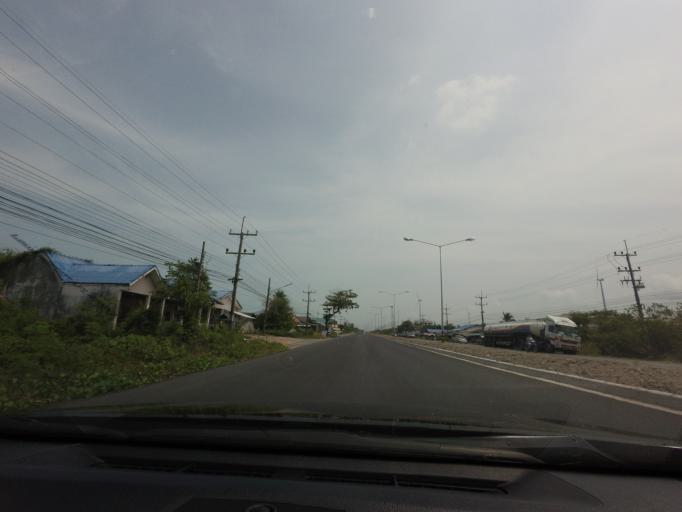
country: TH
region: Songkhla
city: Ranot
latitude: 7.8535
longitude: 100.3509
